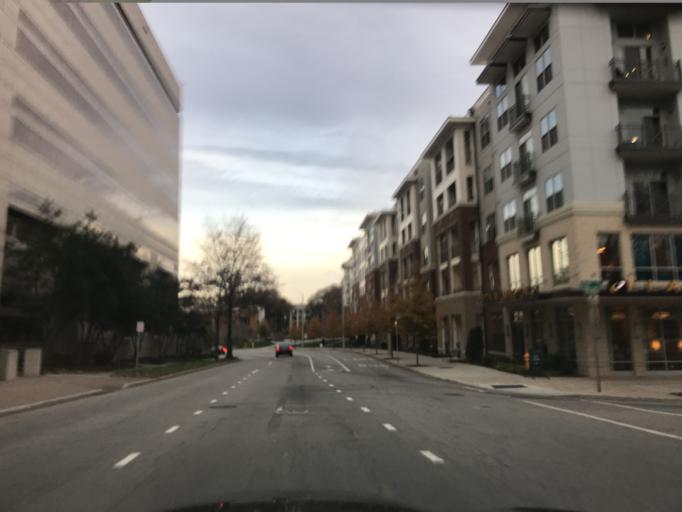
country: US
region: North Carolina
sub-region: Wake County
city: Raleigh
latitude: 35.7859
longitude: -78.6378
